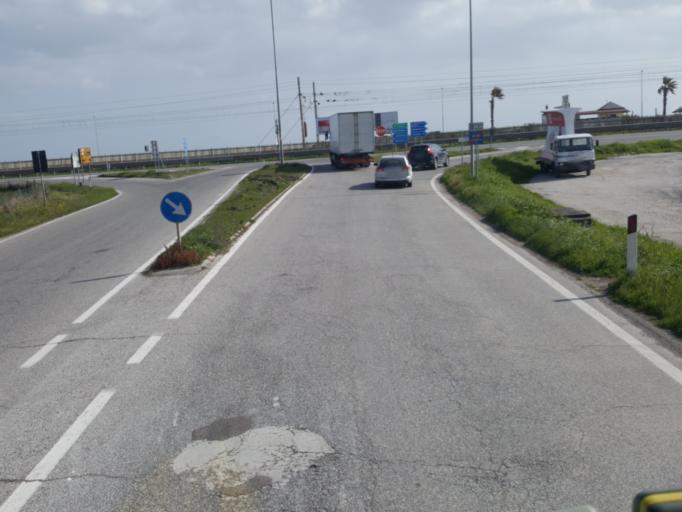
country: IT
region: The Marches
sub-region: Provincia di Macerata
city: Porto Recanati
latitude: 43.4079
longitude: 13.6757
